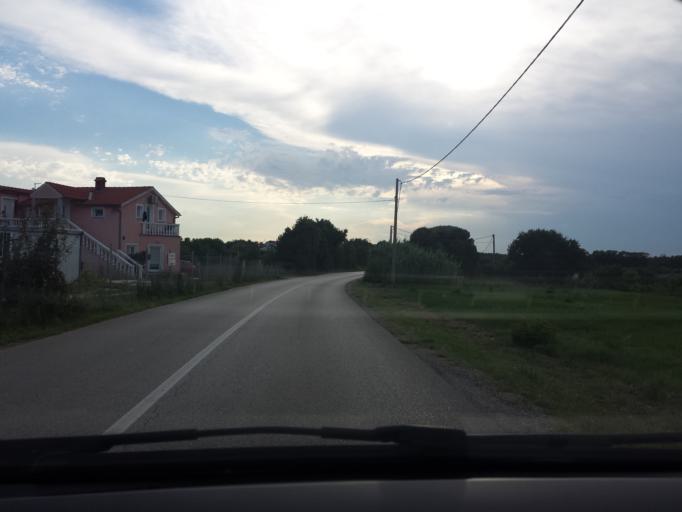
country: HR
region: Istarska
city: Galizana
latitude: 44.9070
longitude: 13.8527
